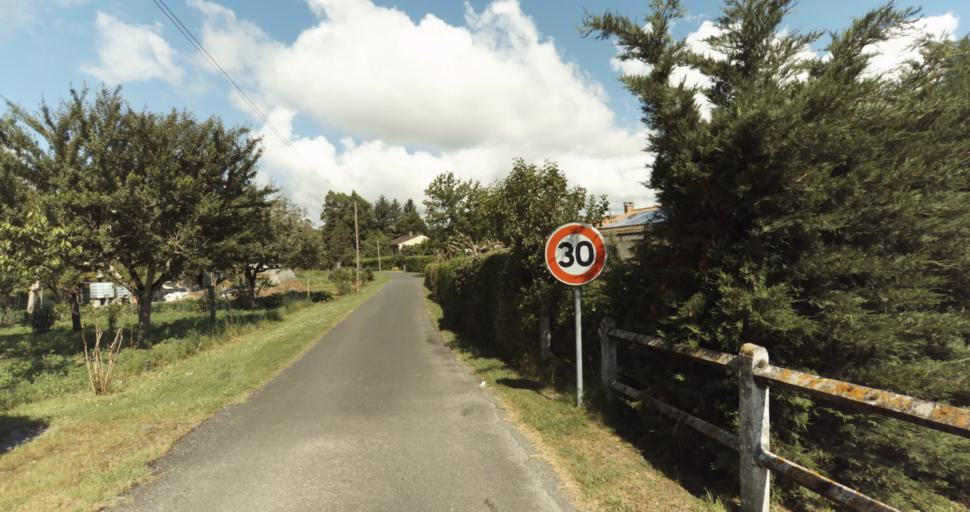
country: FR
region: Aquitaine
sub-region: Departement de la Dordogne
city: Le Bugue
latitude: 44.8458
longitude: 0.9069
